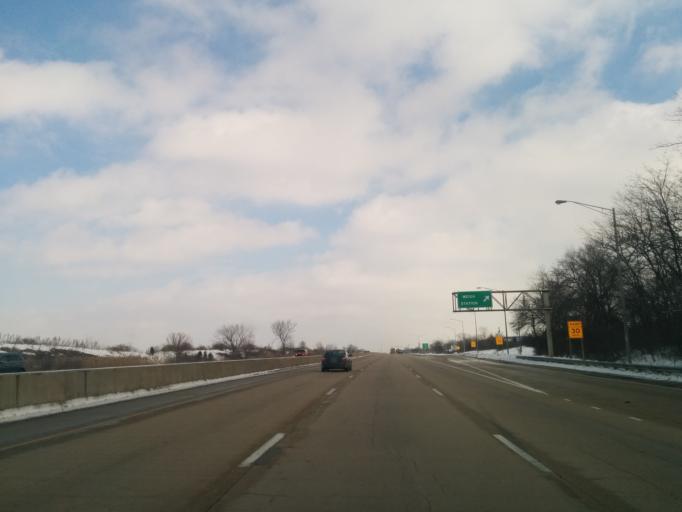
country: US
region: Illinois
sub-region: Will County
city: Mokena
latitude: 41.5521
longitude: -87.9098
